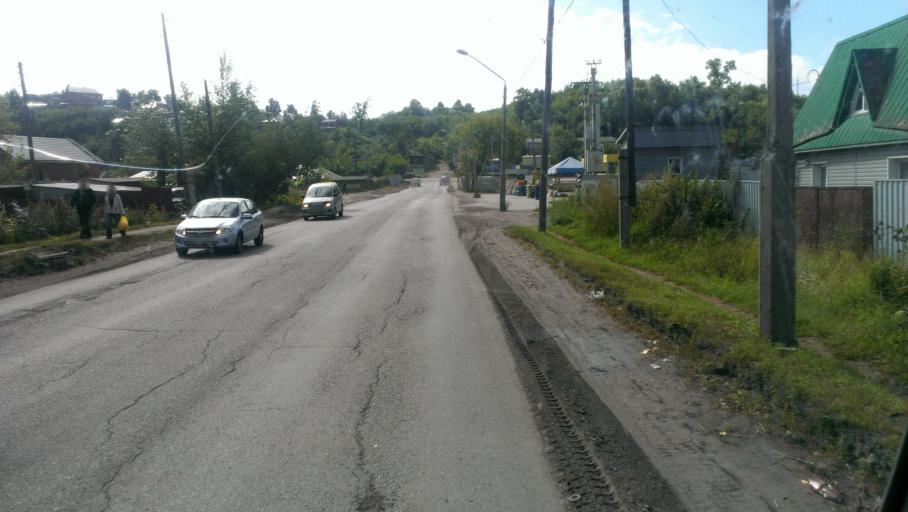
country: RU
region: Altai Krai
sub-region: Gorod Barnaulskiy
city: Barnaul
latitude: 53.3208
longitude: 83.7695
